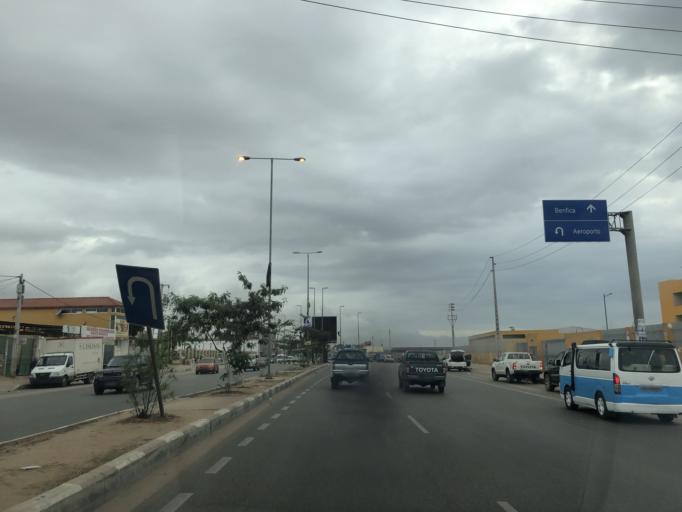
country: AO
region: Luanda
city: Luanda
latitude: -8.8803
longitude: 13.2092
